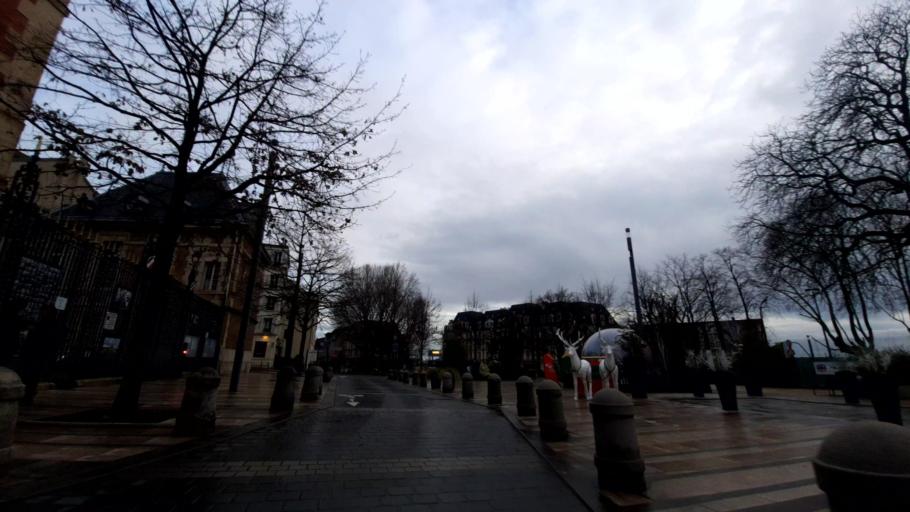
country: FR
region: Ile-de-France
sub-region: Departement du Val-de-Marne
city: Charenton-le-Pont
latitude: 48.8197
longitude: 2.4157
